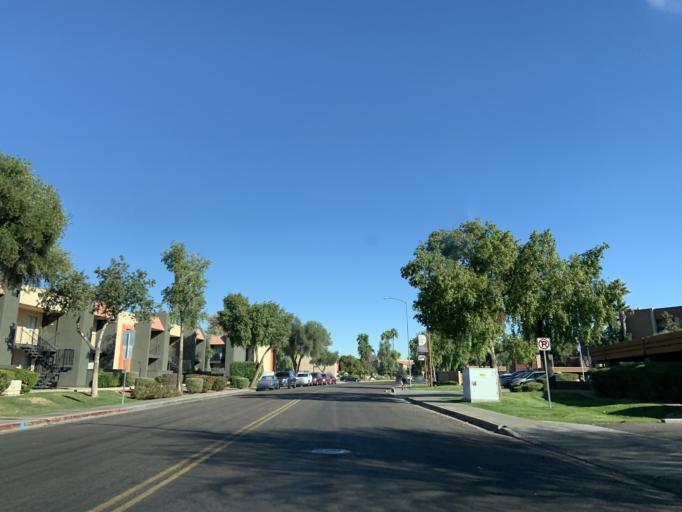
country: US
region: Arizona
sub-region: Maricopa County
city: Tempe
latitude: 33.3984
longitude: -111.8711
